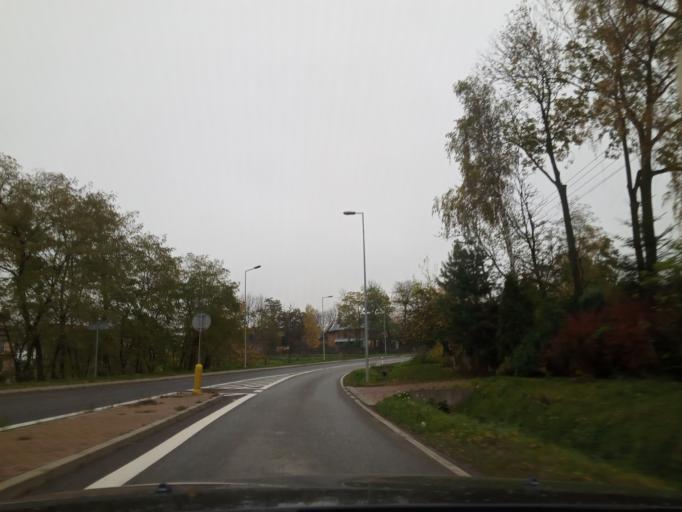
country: PL
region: Lesser Poland Voivodeship
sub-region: Powiat proszowicki
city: Klimontow
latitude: 50.2318
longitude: 20.3641
